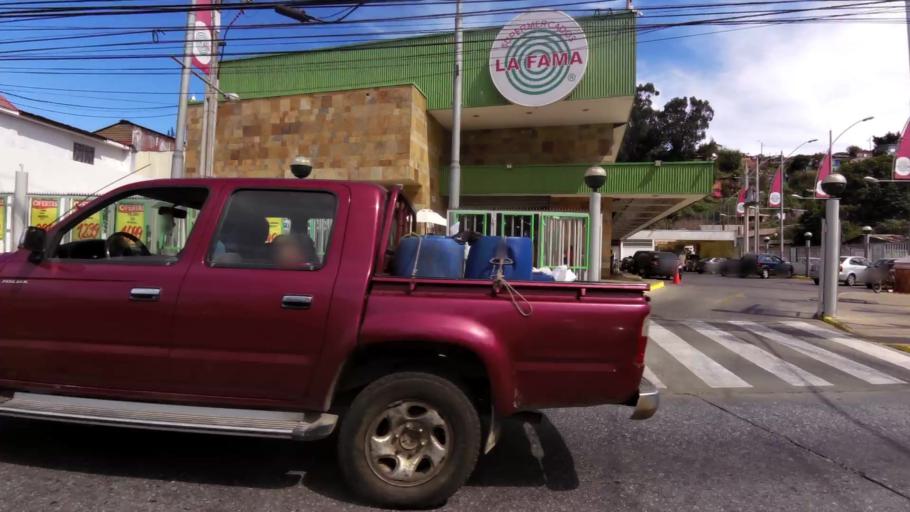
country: CL
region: Biobio
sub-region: Provincia de Concepcion
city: Talcahuano
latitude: -36.7133
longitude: -73.1155
